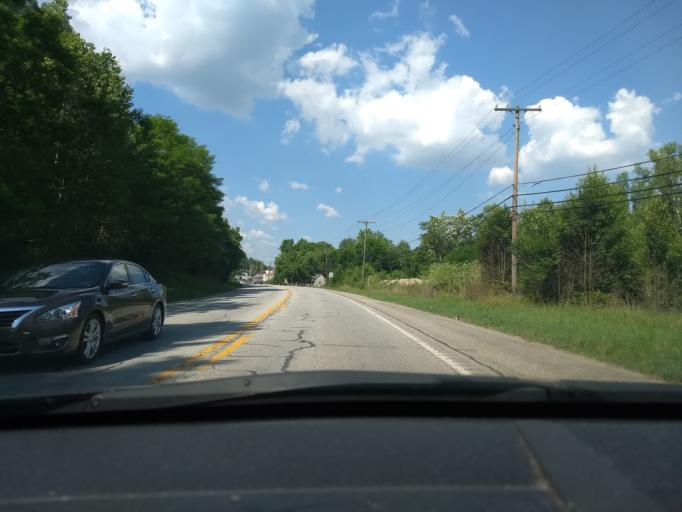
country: US
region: Indiana
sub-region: Floyd County
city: New Albany
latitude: 38.2702
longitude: -85.8419
